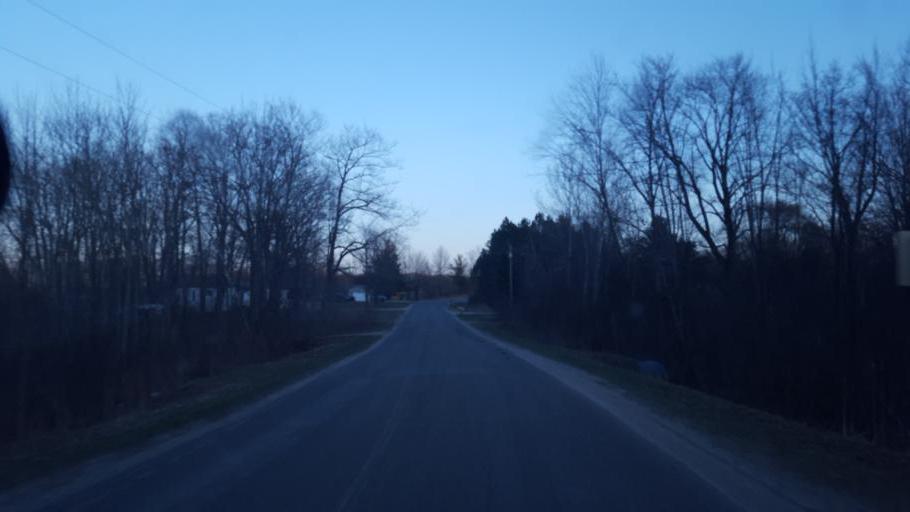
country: US
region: Michigan
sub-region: Montcalm County
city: Howard City
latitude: 43.5369
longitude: -85.4844
